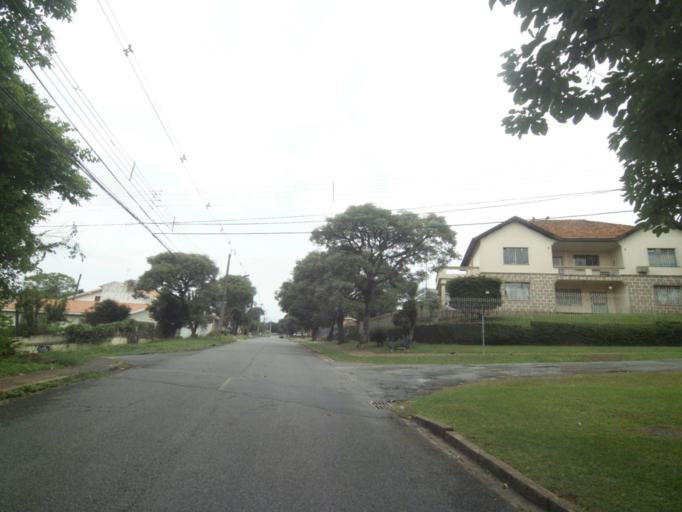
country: BR
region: Parana
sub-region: Curitiba
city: Curitiba
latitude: -25.4119
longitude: -49.2888
